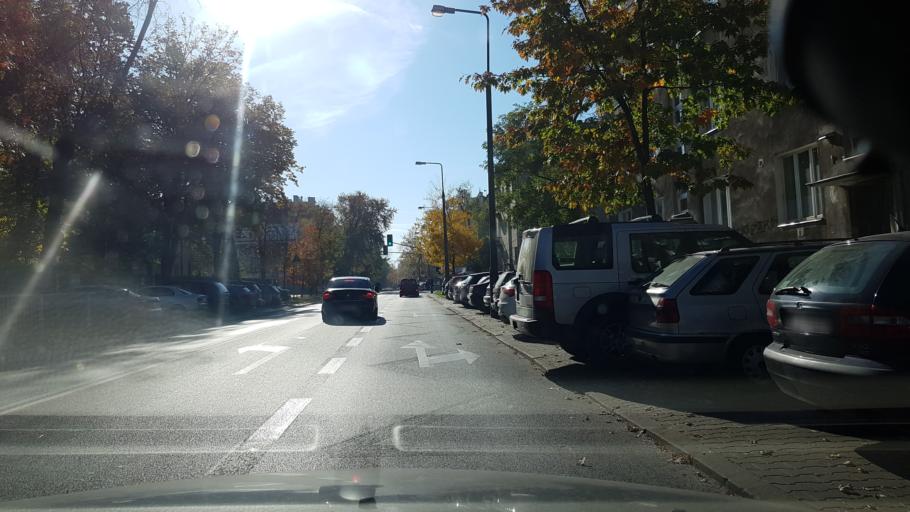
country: PL
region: Masovian Voivodeship
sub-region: Warszawa
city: Mokotow
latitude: 52.1999
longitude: 21.0177
